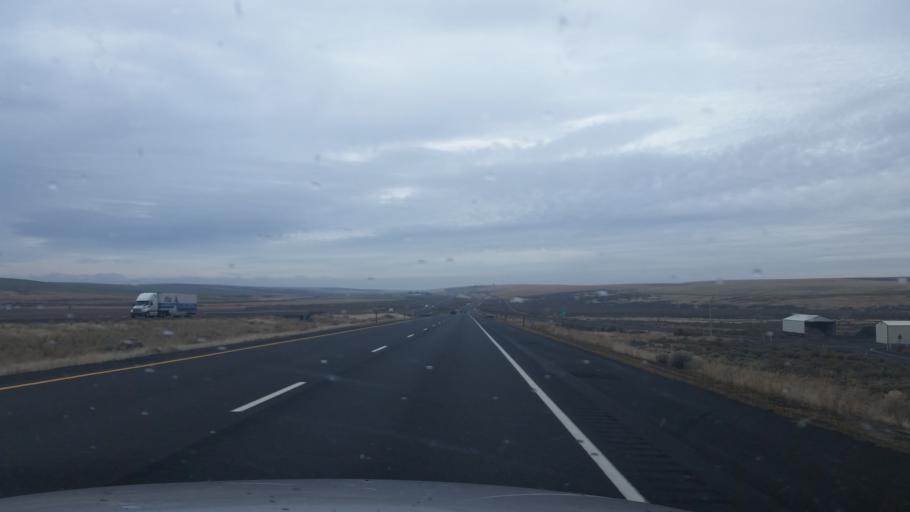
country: US
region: Washington
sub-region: Grant County
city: Warden
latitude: 47.0873
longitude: -118.8724
